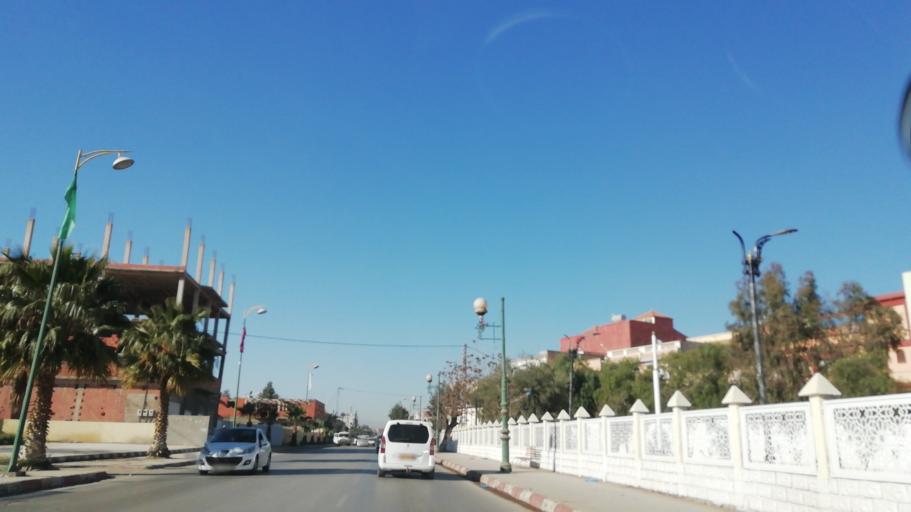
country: DZ
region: Tlemcen
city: Nedroma
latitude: 34.8455
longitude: -1.7421
